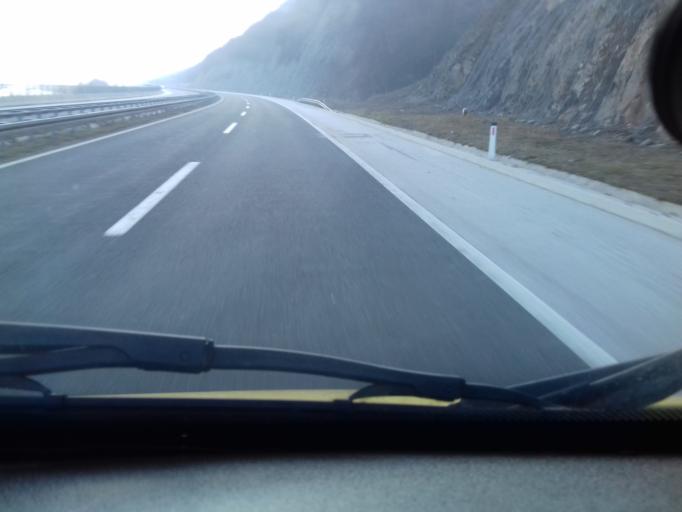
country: BA
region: Federation of Bosnia and Herzegovina
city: Dobrinje
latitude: 44.0640
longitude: 18.1040
